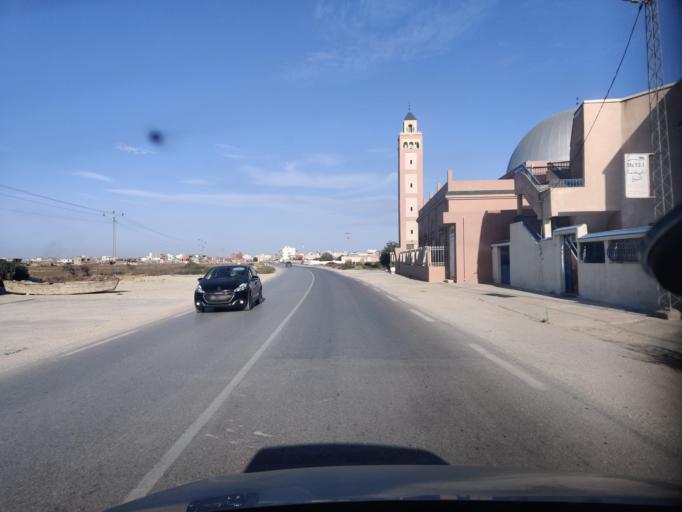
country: TN
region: Ariana
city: Ariana
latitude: 36.9542
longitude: 10.2313
